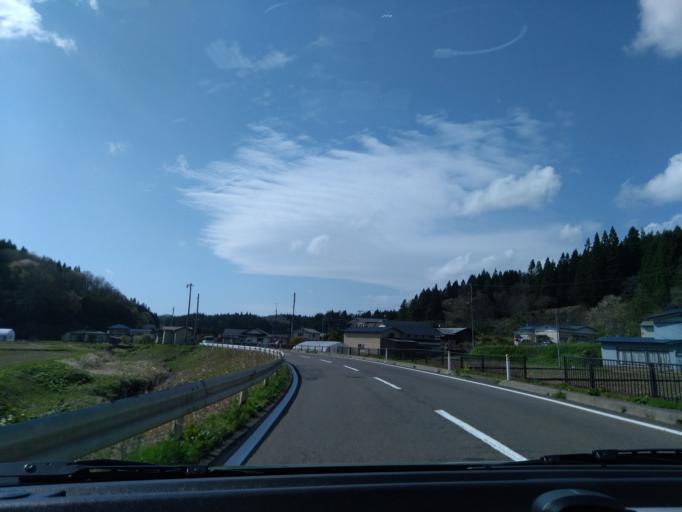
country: JP
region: Akita
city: Akita
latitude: 39.7112
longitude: 140.2036
